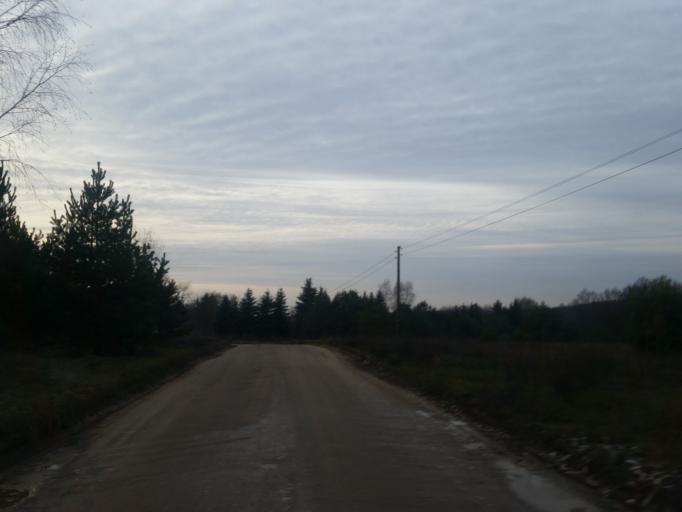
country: PL
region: Kujawsko-Pomorskie
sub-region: Powiat brodnicki
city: Brodnica
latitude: 53.2221
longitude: 19.3483
